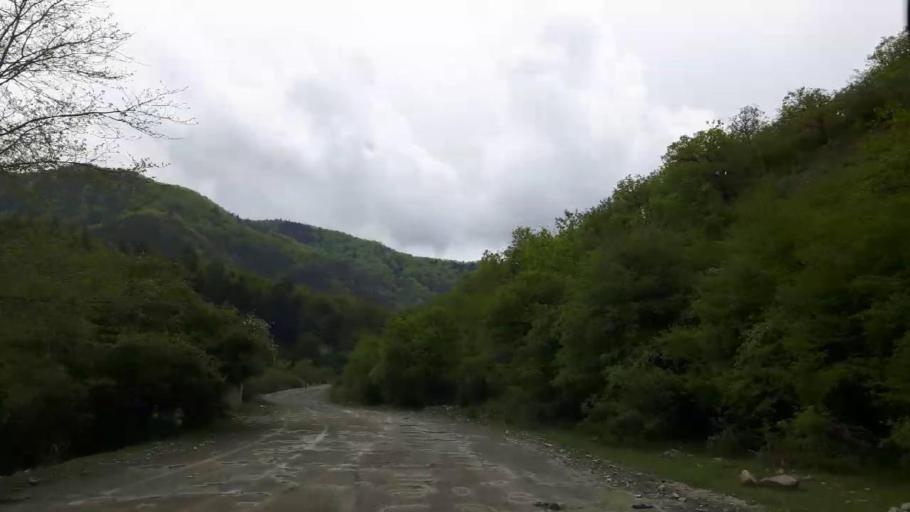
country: GE
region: Shida Kartli
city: Gori
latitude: 41.8705
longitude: 43.9854
